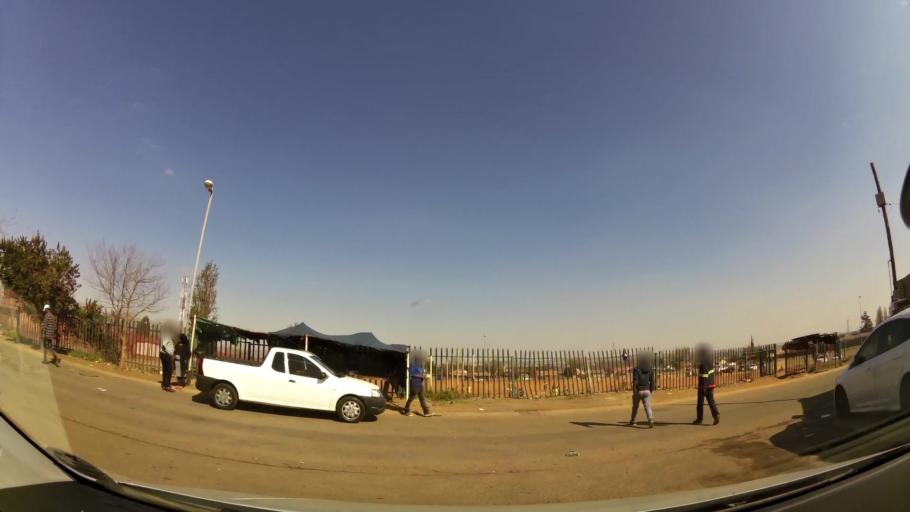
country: ZA
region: Gauteng
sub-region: City of Johannesburg Metropolitan Municipality
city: Soweto
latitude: -26.2852
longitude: 27.8583
